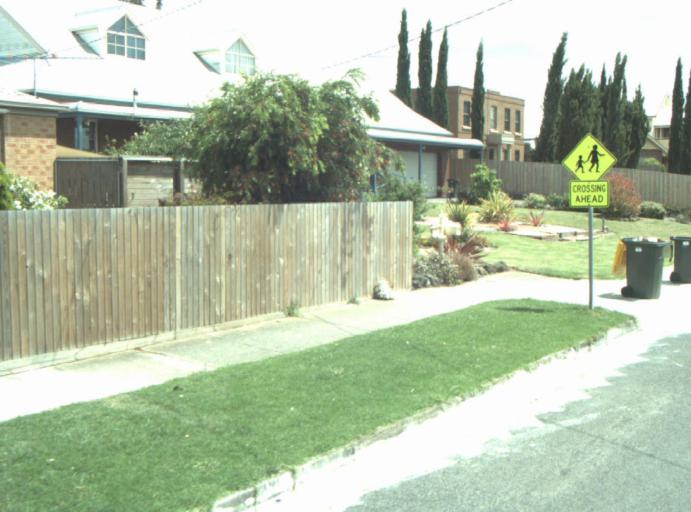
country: AU
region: Victoria
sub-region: Greater Geelong
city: Wandana Heights
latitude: -38.1861
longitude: 144.3102
